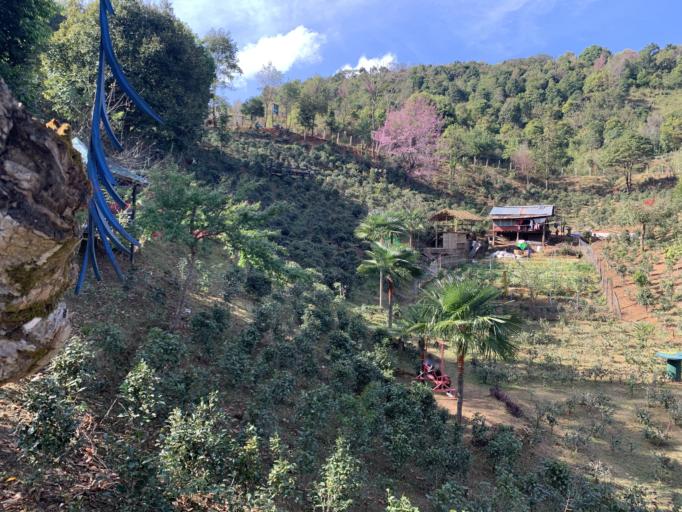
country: MM
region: Mandalay
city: Mogok
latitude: 22.9666
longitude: 96.5603
